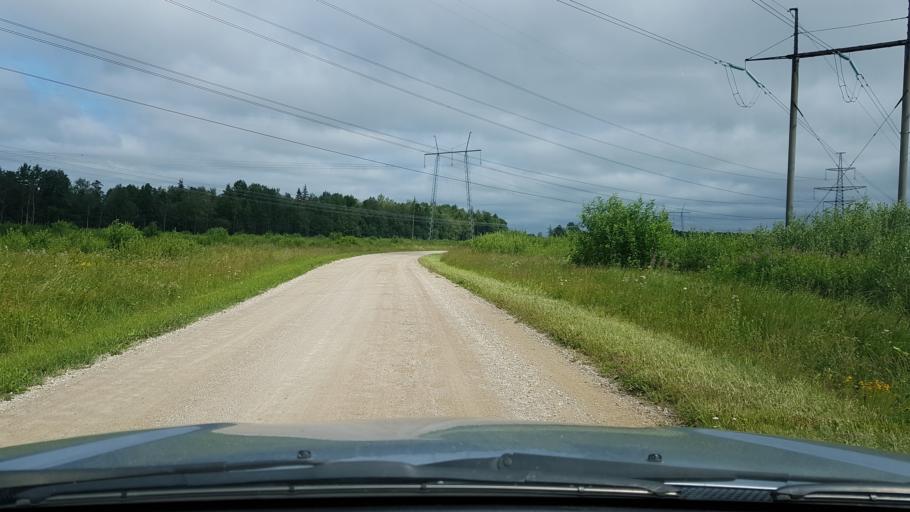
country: EE
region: Ida-Virumaa
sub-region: Narva-Joesuu linn
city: Narva-Joesuu
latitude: 59.3639
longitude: 28.0643
